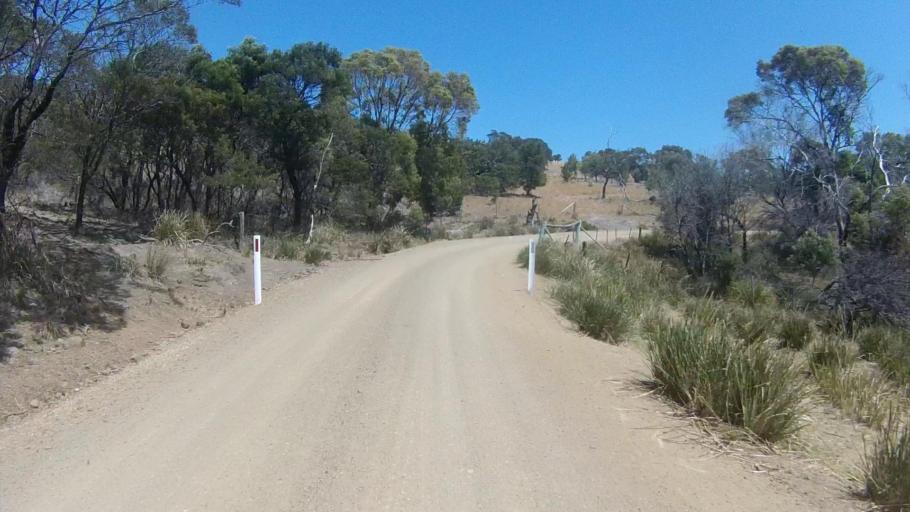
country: AU
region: Tasmania
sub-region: Sorell
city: Sorell
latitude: -42.8924
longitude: 147.8458
